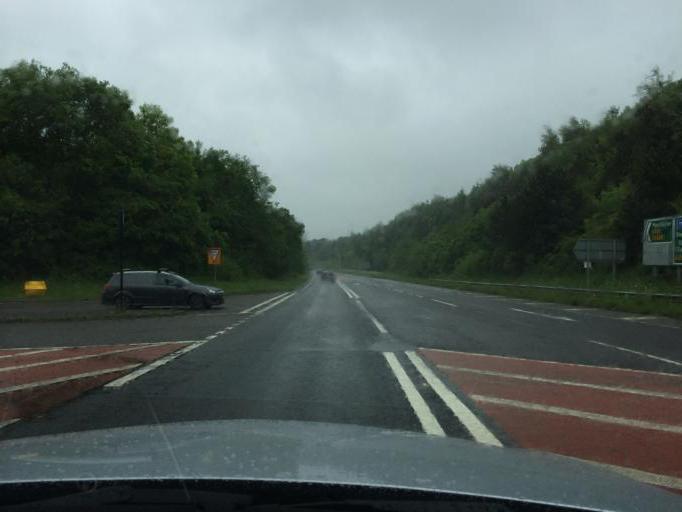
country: GB
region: England
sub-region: Sheffield
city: Stocksbridge
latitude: 53.4914
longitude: -1.6182
